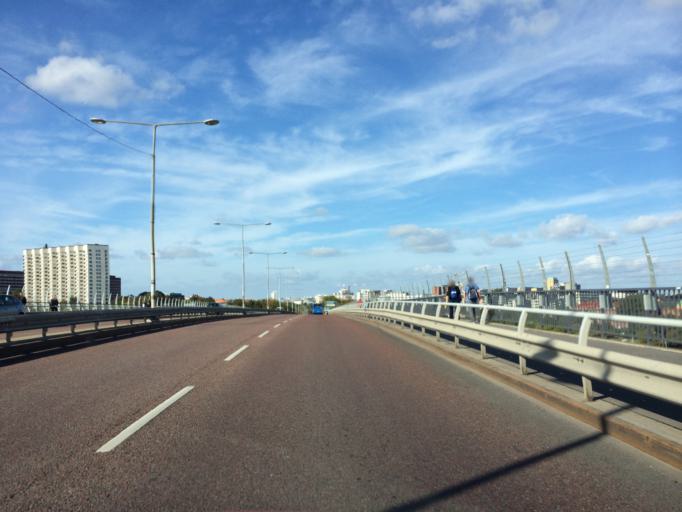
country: SE
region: Stockholm
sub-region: Stockholms Kommun
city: Arsta
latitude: 59.3237
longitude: 18.0283
